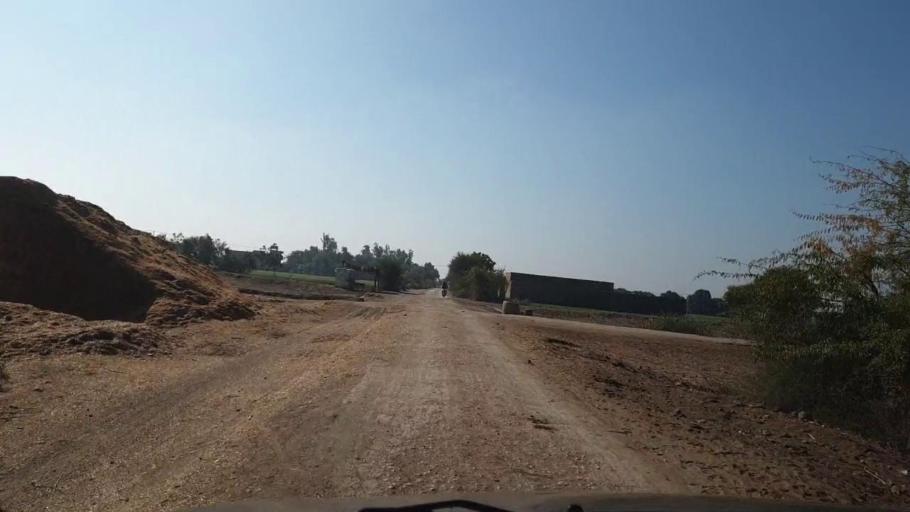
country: PK
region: Sindh
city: Sinjhoro
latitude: 25.9780
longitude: 68.7441
